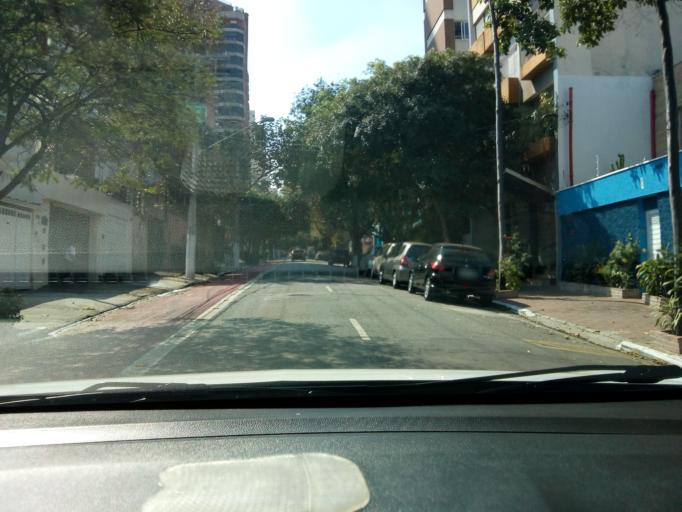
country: BR
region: Sao Paulo
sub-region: Sao Paulo
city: Sao Paulo
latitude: -23.5891
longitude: -46.6462
